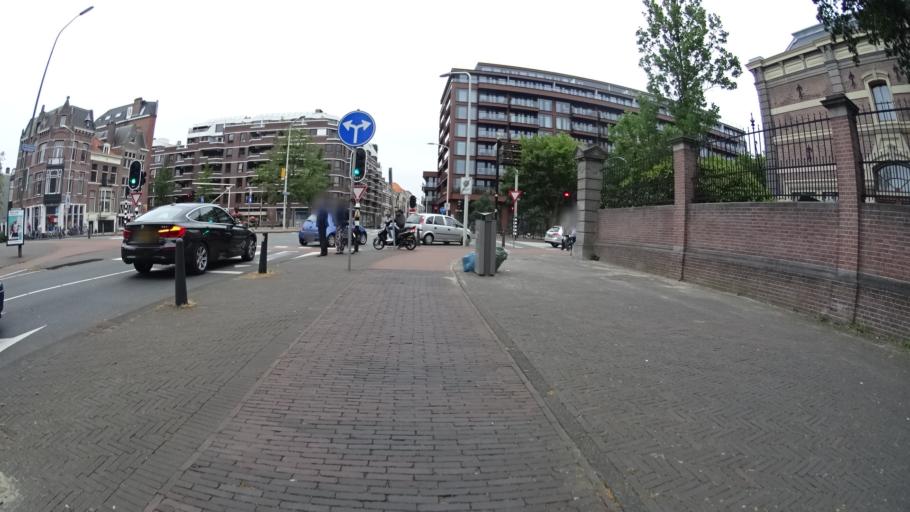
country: NL
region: South Holland
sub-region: Gemeente Den Haag
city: The Hague
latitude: 52.0824
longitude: 4.3019
